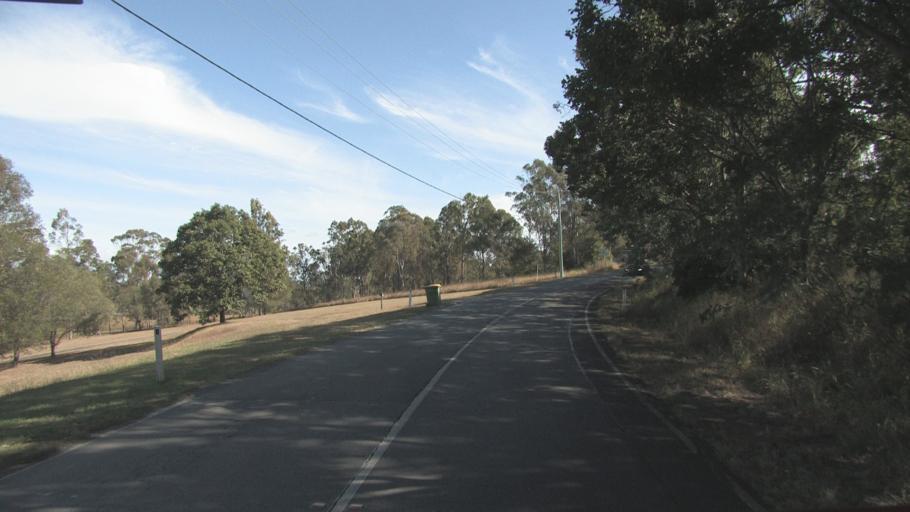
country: AU
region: Queensland
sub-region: Logan
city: Cedar Vale
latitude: -27.8811
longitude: 152.9891
